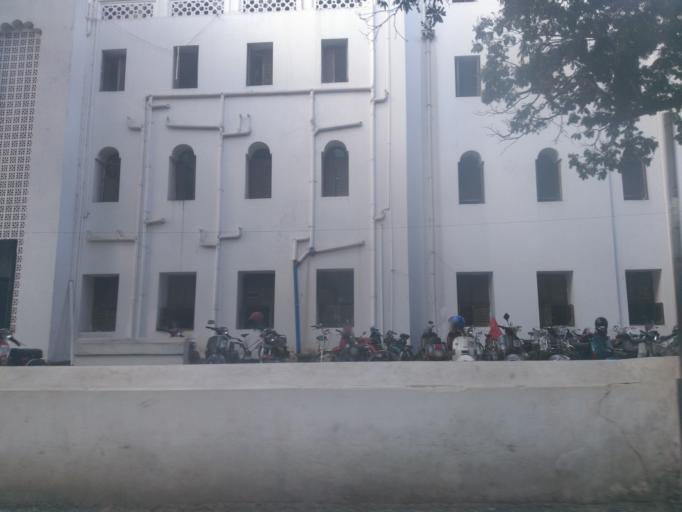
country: TZ
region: Zanzibar Urban/West
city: Zanzibar
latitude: -6.1678
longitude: 39.1902
